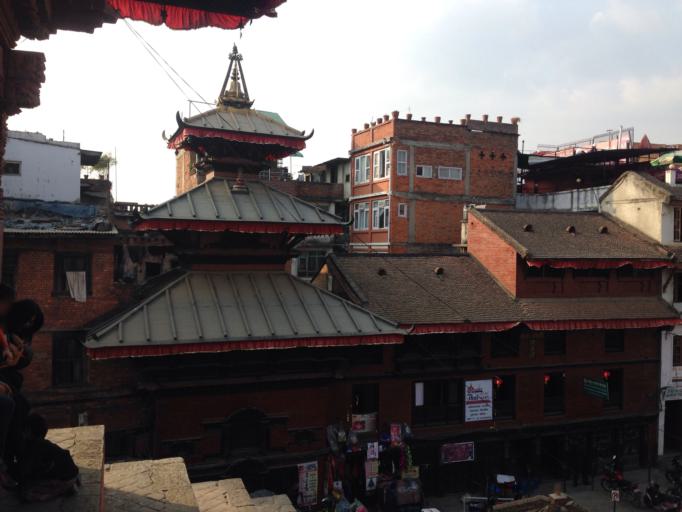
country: NP
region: Central Region
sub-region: Bagmati Zone
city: Kathmandu
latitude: 27.7044
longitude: 85.3062
